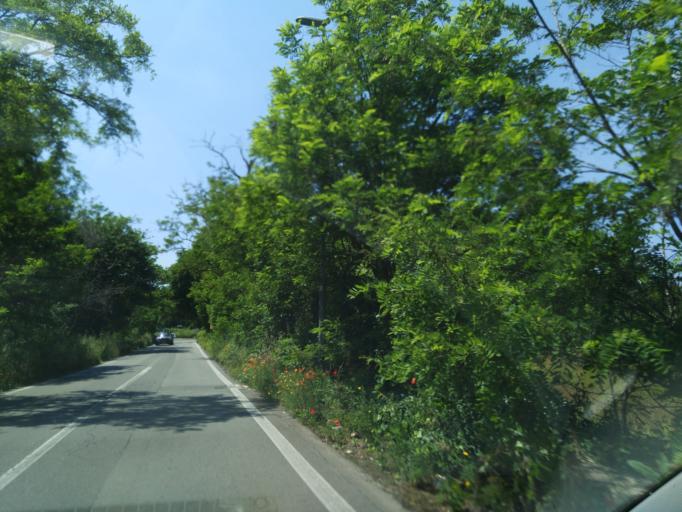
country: IT
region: Latium
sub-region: Citta metropolitana di Roma Capitale
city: Selcetta
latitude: 41.8069
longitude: 12.4587
